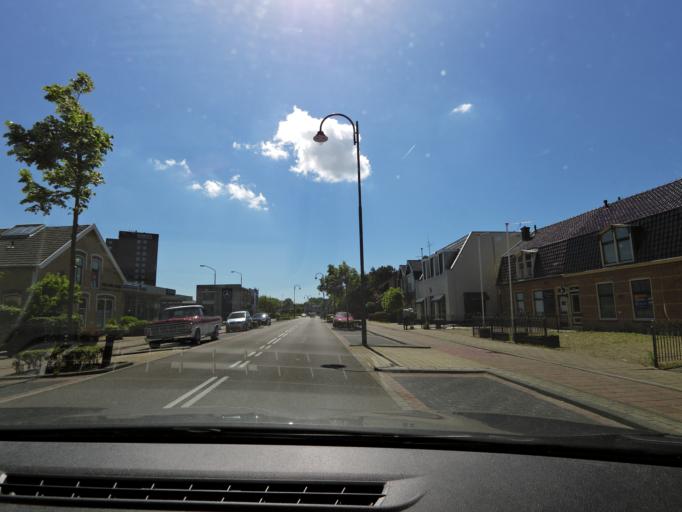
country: NL
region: South Holland
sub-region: Gemeente Hellevoetsluis
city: Hellevoetsluis
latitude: 51.8357
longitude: 4.1324
